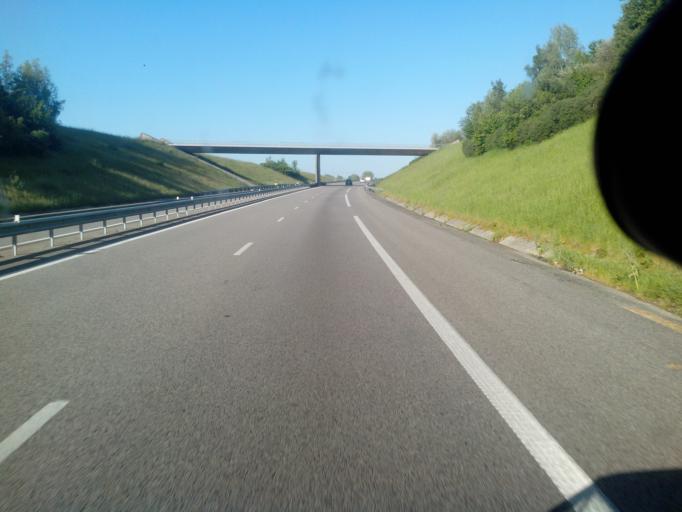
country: FR
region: Haute-Normandie
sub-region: Departement de la Seine-Maritime
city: Nointot
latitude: 49.6019
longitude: 0.4630
